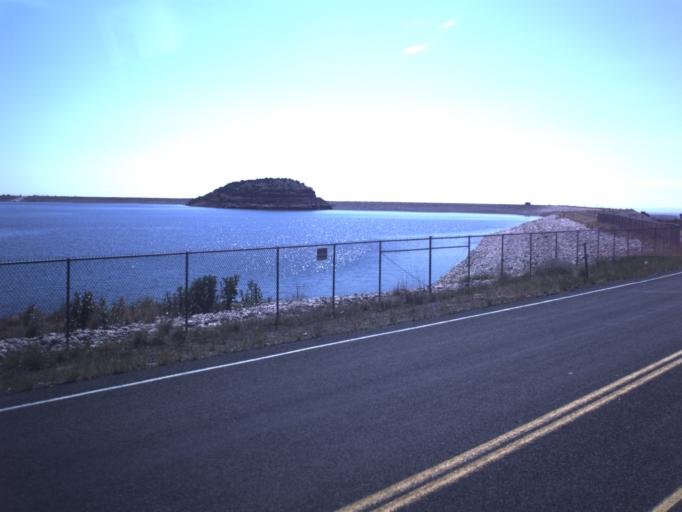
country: US
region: Utah
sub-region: Duchesne County
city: Duchesne
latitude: 40.2986
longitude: -110.2373
